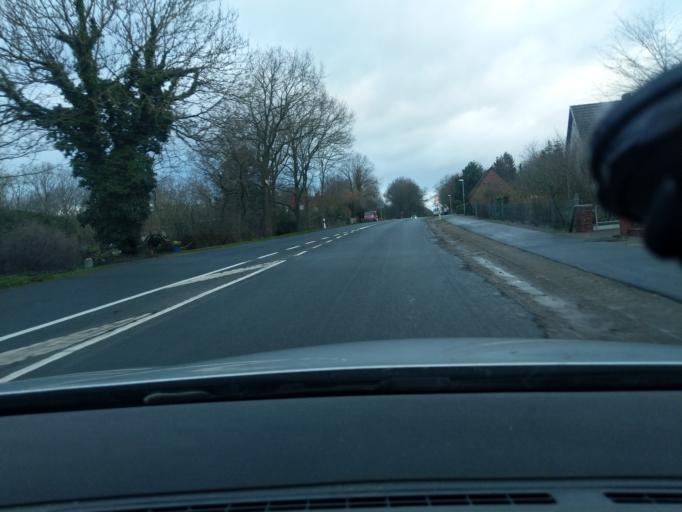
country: DE
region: Lower Saxony
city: Midlum
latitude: 53.7350
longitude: 8.6155
